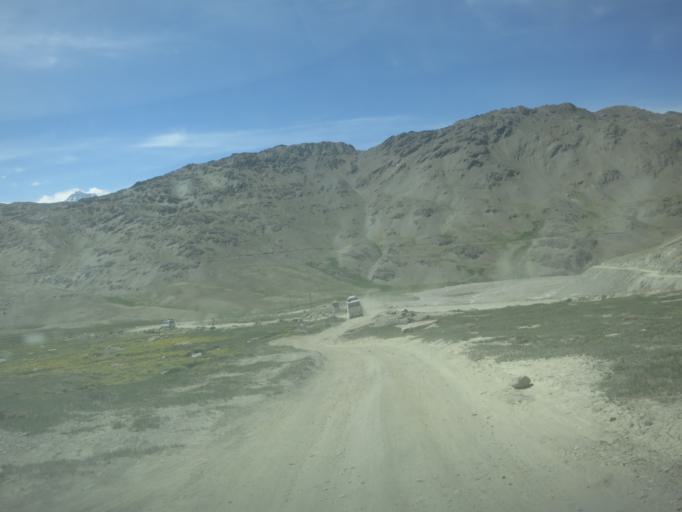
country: IN
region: Himachal Pradesh
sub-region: Kulu
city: Manali
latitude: 32.4050
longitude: 77.6443
